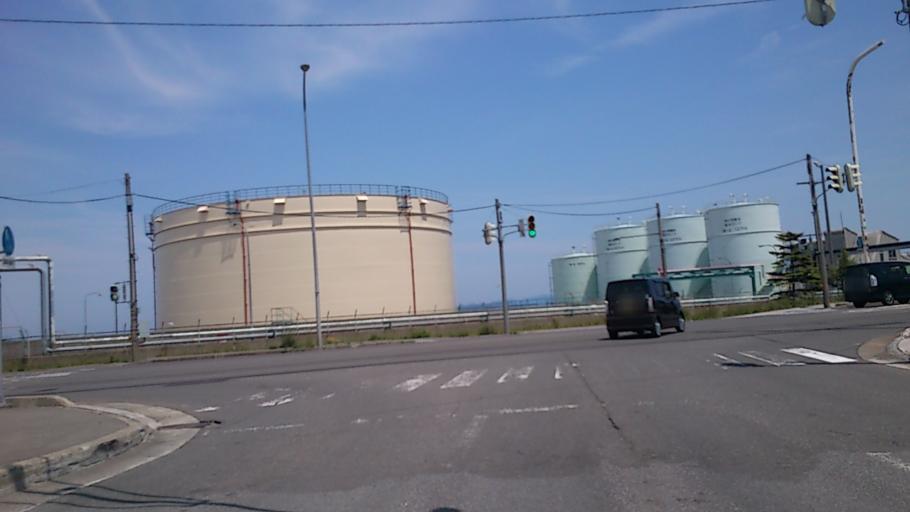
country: JP
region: Aomori
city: Aomori Shi
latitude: 40.8355
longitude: 140.7260
